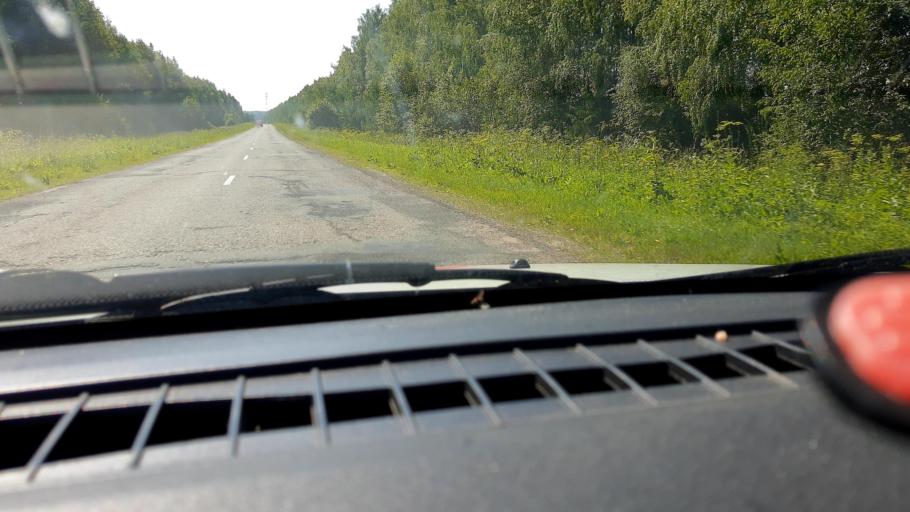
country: RU
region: Nizjnij Novgorod
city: Sharanga
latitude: 57.0688
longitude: 46.5408
